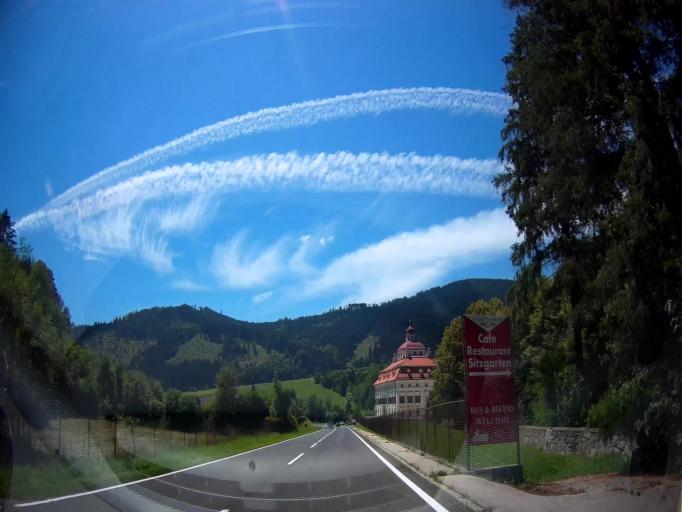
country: AT
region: Carinthia
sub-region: Politischer Bezirk Sankt Veit an der Glan
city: Althofen
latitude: 46.8935
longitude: 14.4477
